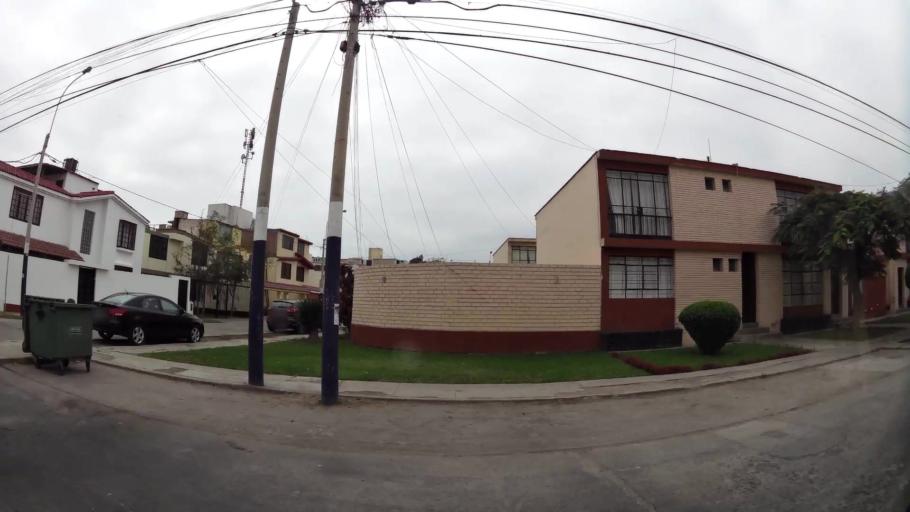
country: PE
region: Lima
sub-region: Lima
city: Surco
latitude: -12.1570
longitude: -77.0209
